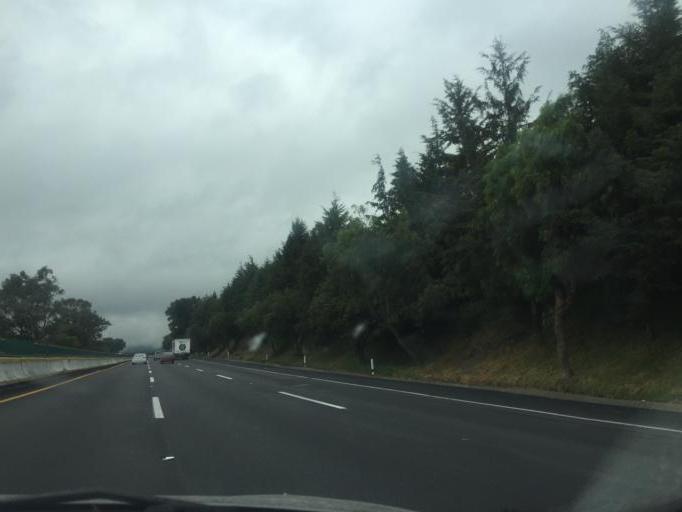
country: MX
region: Mexico City
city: Xochimilco
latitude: 19.2279
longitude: -99.1310
